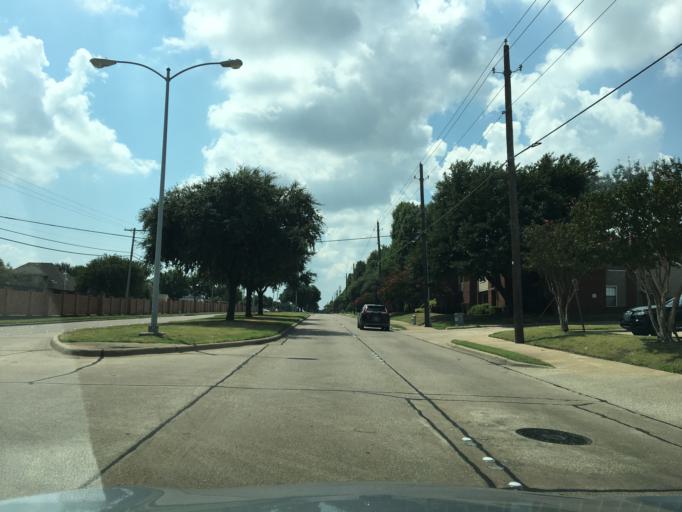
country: US
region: Texas
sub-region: Dallas County
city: Garland
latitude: 32.9441
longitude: -96.6482
